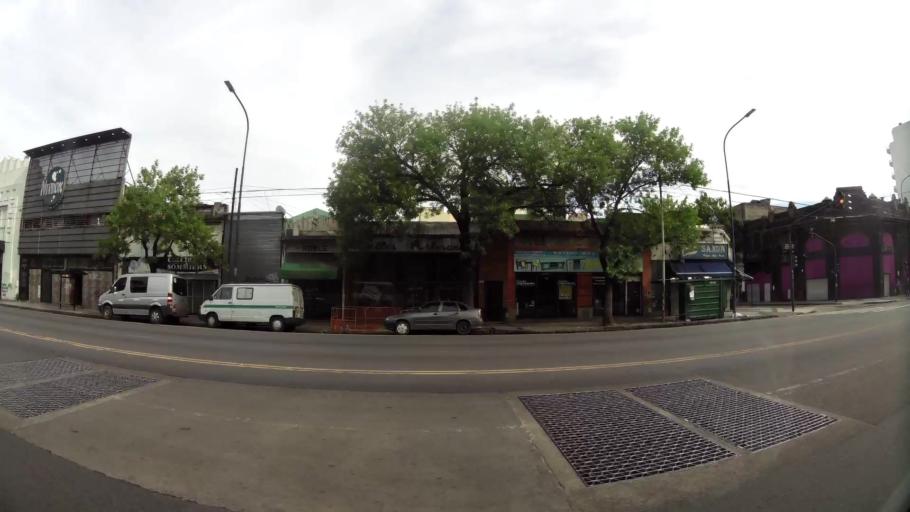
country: AR
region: Buenos Aires F.D.
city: Villa Santa Rita
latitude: -34.6320
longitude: -58.4743
